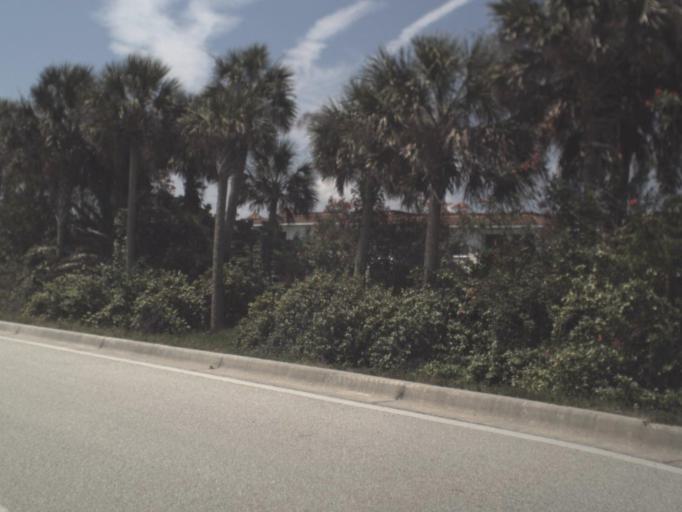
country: US
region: Florida
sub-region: Saint Johns County
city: Villano Beach
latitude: 29.9676
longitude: -81.3103
